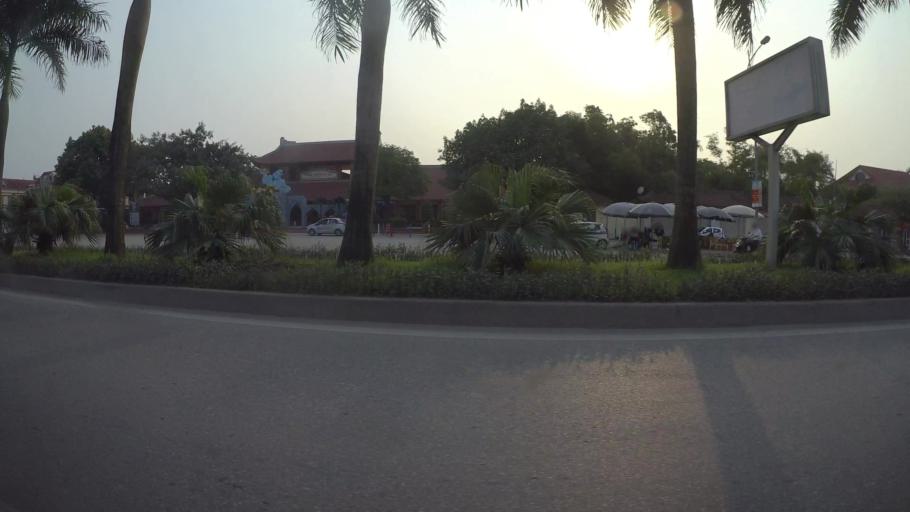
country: VN
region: Ha Noi
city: Cau Dien
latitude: 20.9993
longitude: 105.7340
